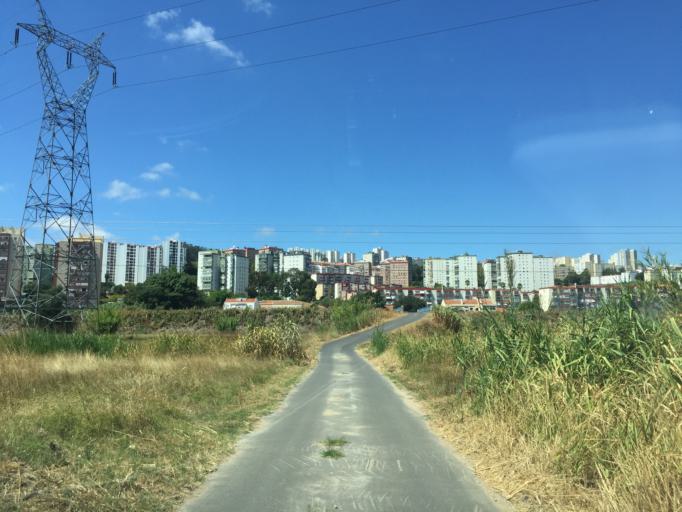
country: PT
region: Lisbon
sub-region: Odivelas
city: Povoa de Santo Adriao
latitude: 38.8086
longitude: -9.1537
